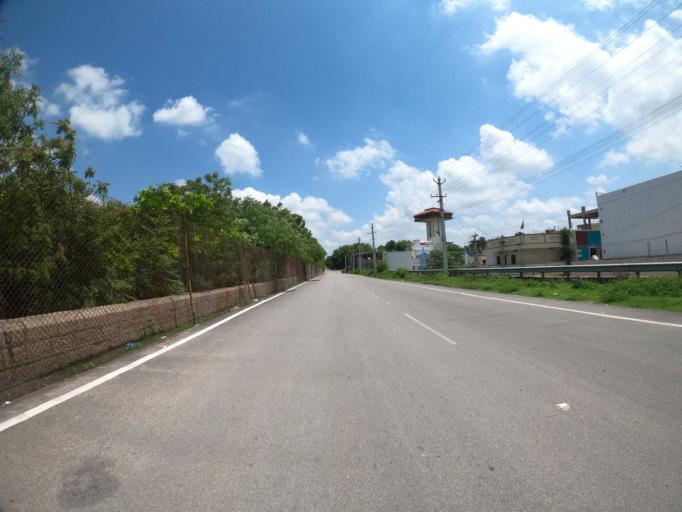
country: IN
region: Telangana
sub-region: Medak
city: Serilingampalle
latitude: 17.3870
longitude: 78.3164
